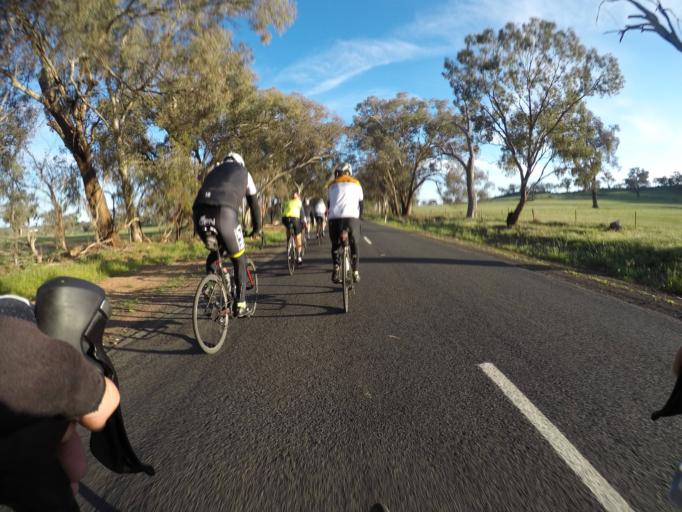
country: AU
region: New South Wales
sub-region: Cabonne
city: Molong
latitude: -33.0472
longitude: 148.8169
